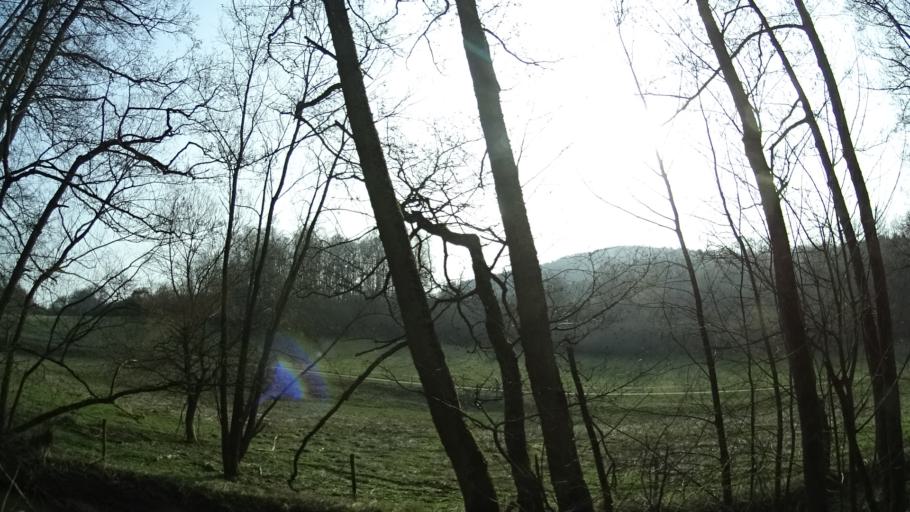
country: DE
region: Rheinland-Pfalz
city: Niederstaufenbach
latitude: 49.5360
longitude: 7.5091
